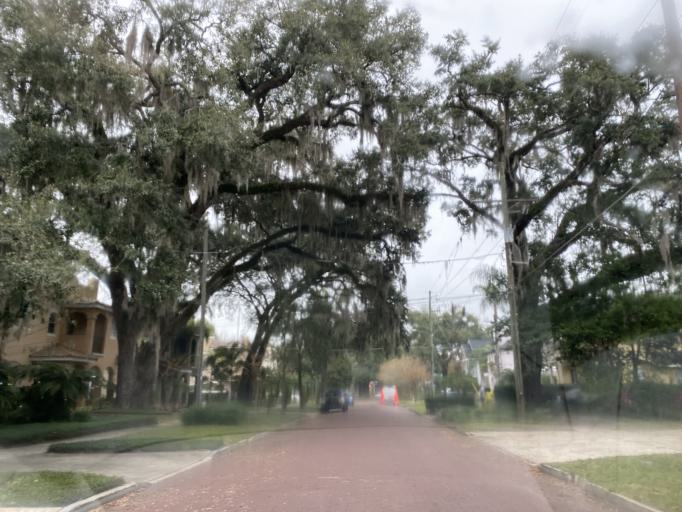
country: US
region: Florida
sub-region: Orange County
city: Orlando
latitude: 28.5561
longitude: -81.3947
